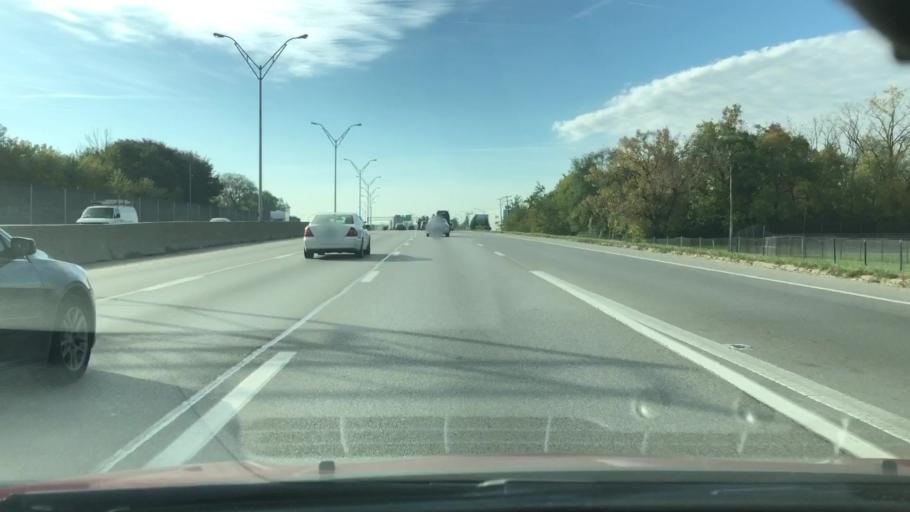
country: US
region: Ohio
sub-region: Franklin County
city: Columbus
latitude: 40.0212
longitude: -82.9953
